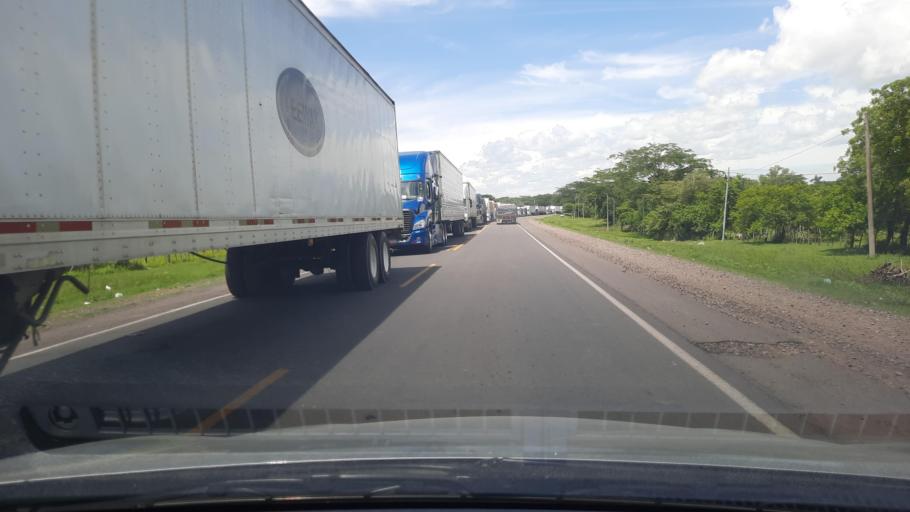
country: NI
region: Chinandega
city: Somotillo
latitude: 13.0592
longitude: -86.9333
